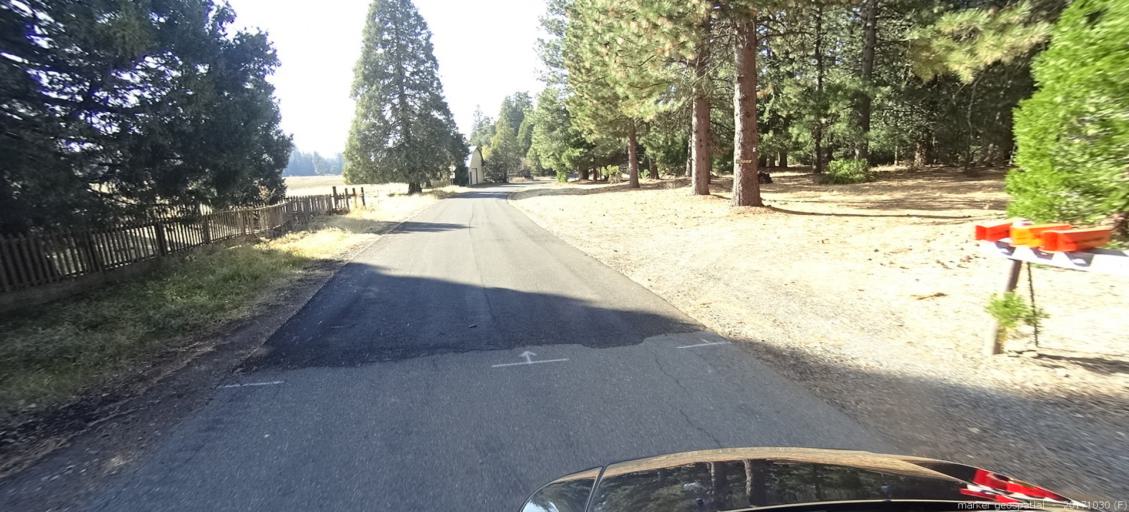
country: US
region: California
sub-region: Shasta County
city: Shingletown
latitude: 40.5306
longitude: -121.6869
